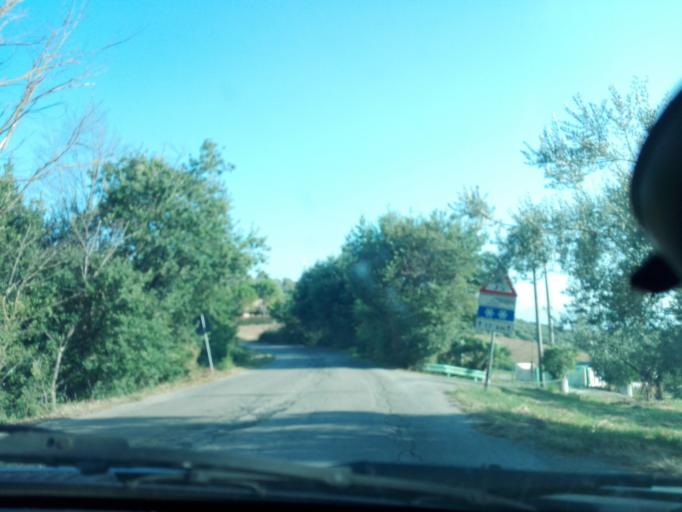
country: IT
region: Abruzzo
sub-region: Provincia di Pescara
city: Cappelle sul Tavo
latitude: 42.4453
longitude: 14.0922
